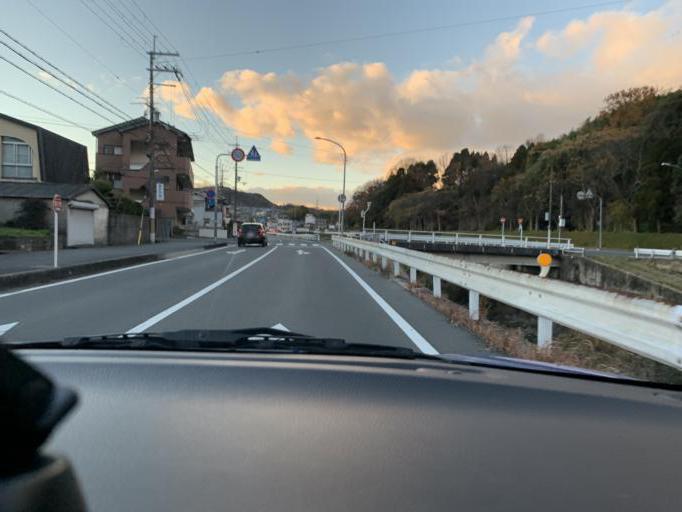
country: JP
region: Nara
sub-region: Ikoma-shi
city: Ikoma
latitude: 34.7109
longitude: 135.7281
